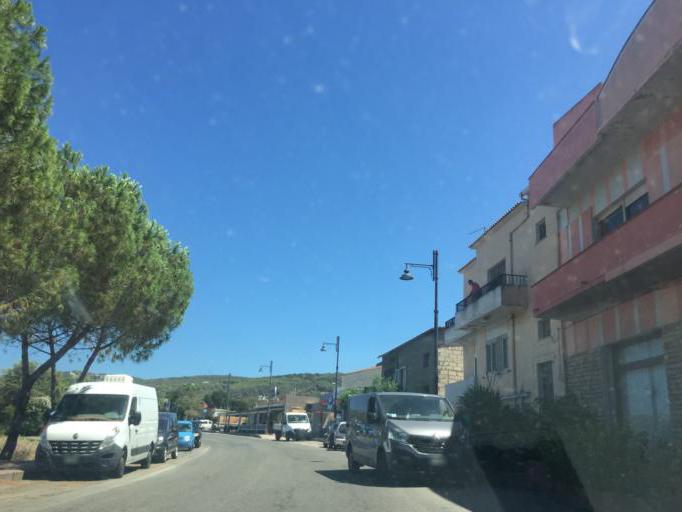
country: IT
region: Sardinia
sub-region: Provincia di Sassari
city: Castelsardo
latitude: 40.9118
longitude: 8.7175
